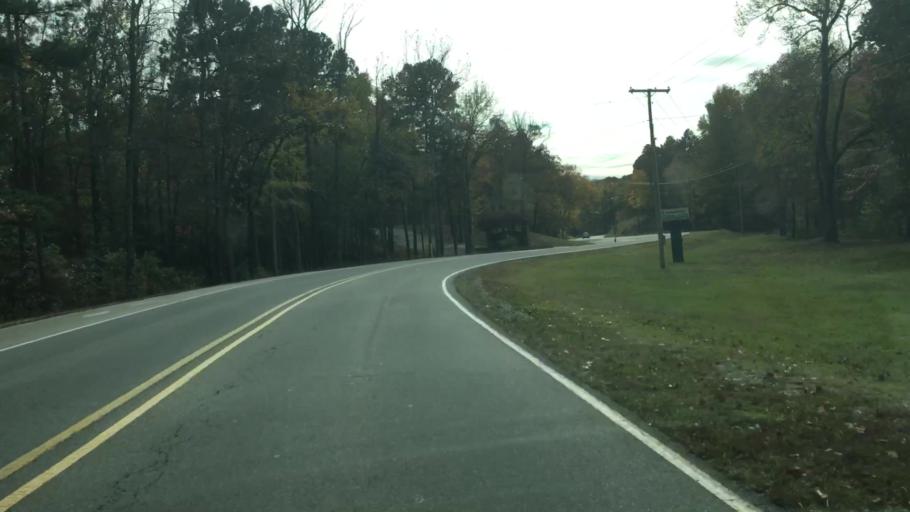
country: US
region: Arkansas
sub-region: Pulaski County
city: North Little Rock
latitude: 34.8183
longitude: -92.2889
